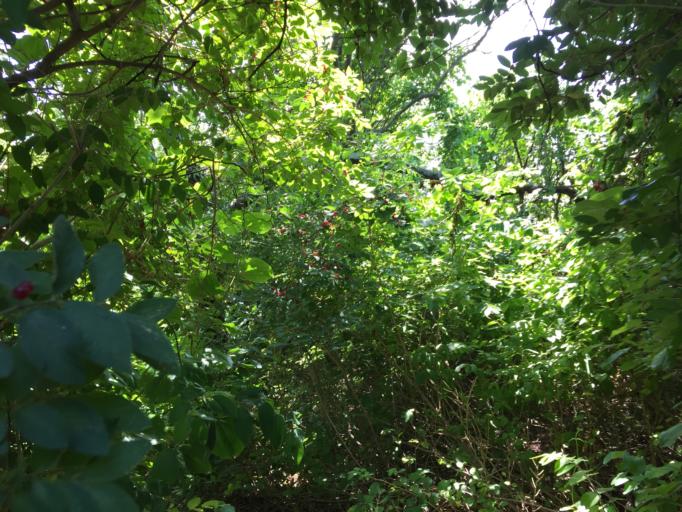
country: US
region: New York
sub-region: Suffolk County
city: Montauk
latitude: 41.0589
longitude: -71.8951
